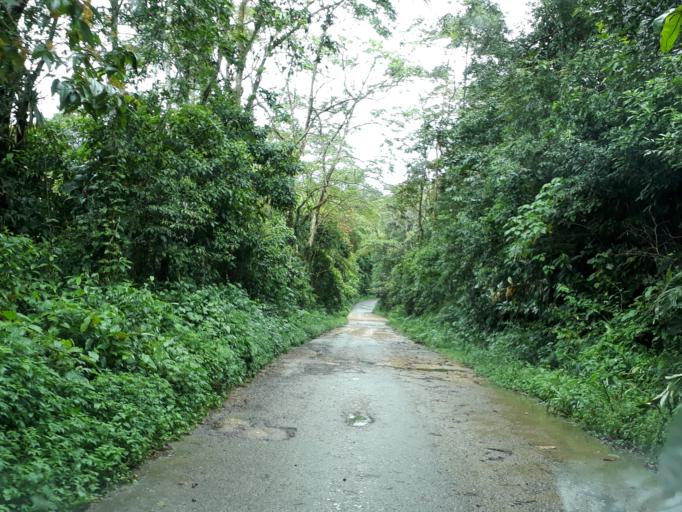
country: CO
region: Boyaca
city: Santa Maria
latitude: 4.6869
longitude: -73.3104
